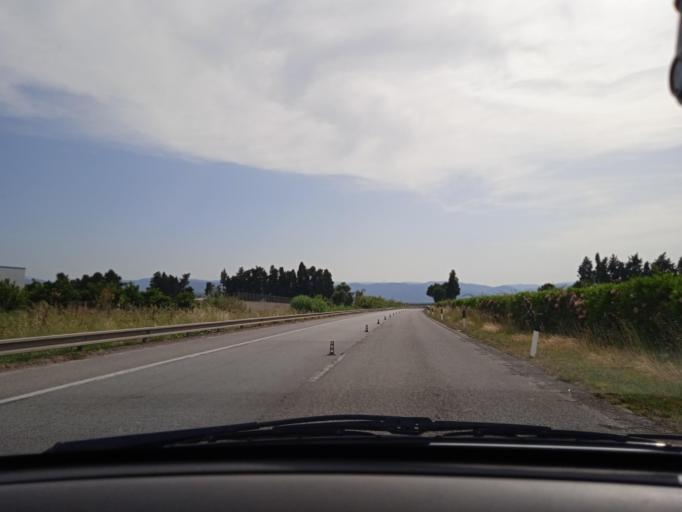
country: IT
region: Sicily
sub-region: Messina
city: Terme
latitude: 38.1446
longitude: 15.1660
